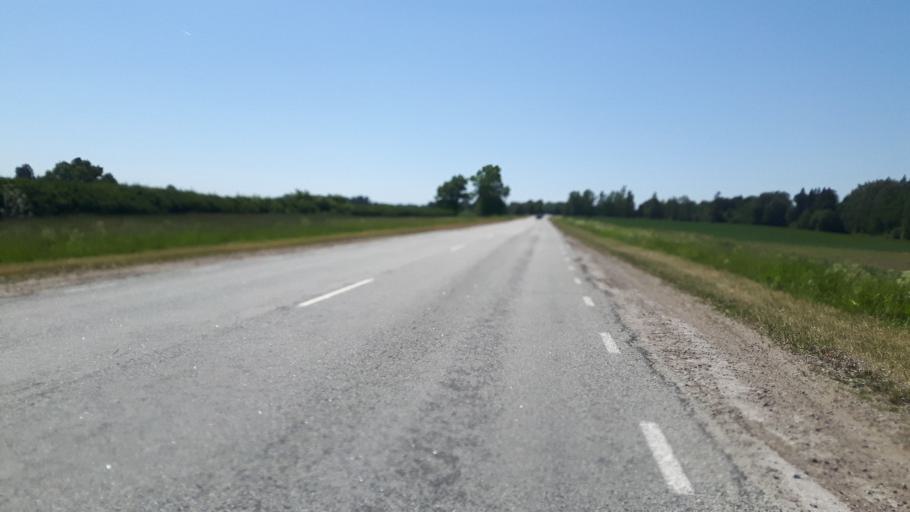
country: EE
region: Paernumaa
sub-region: Sindi linn
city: Sindi
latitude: 58.4446
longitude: 24.7591
